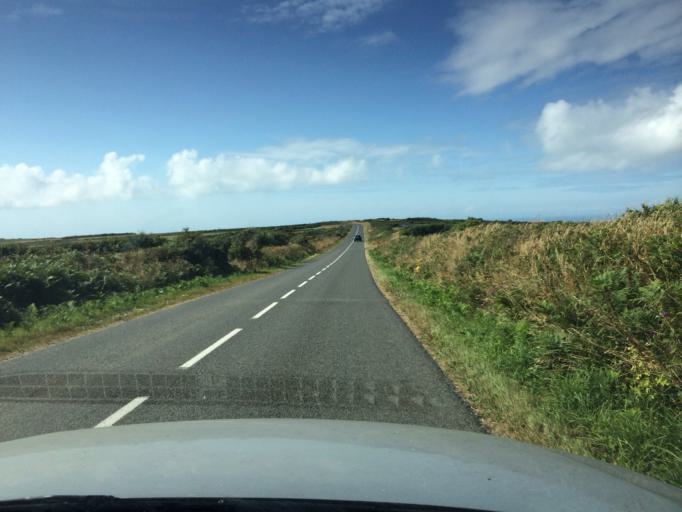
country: FR
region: Lower Normandy
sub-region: Departement de la Manche
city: Beaumont-Hague
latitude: 49.6903
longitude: -1.9147
